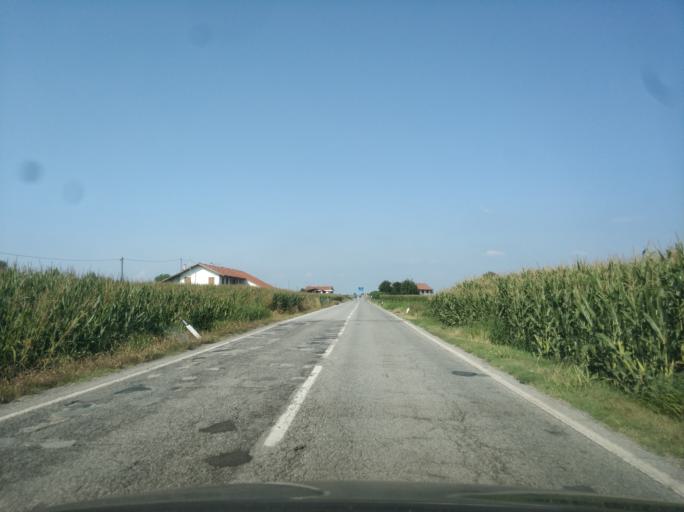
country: IT
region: Piedmont
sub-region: Provincia di Cuneo
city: Centallo
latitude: 44.5311
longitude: 7.6072
